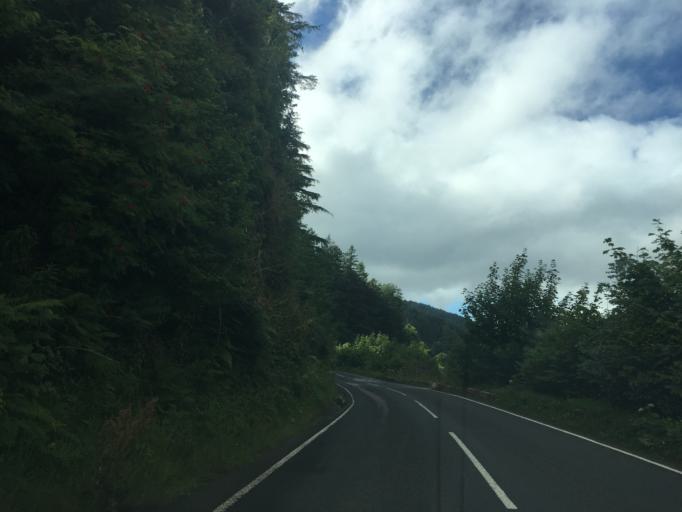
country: GB
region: Scotland
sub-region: Argyll and Bute
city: Ardrishaig
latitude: 56.0743
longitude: -5.5320
